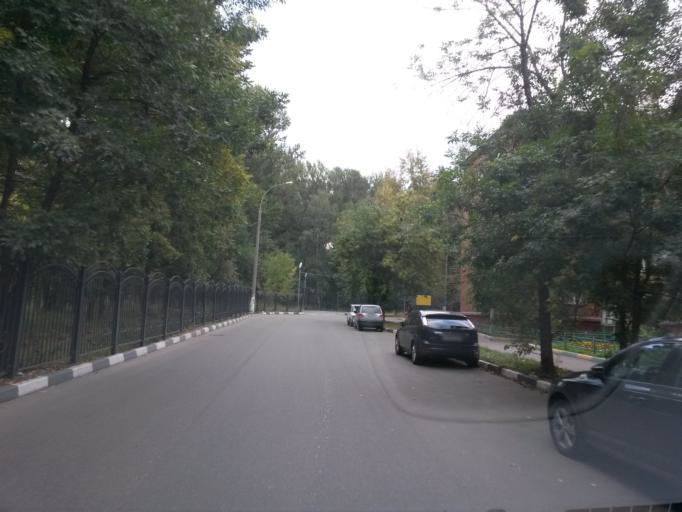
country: RU
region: Moscow
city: Kapotnya
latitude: 55.6397
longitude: 37.8010
